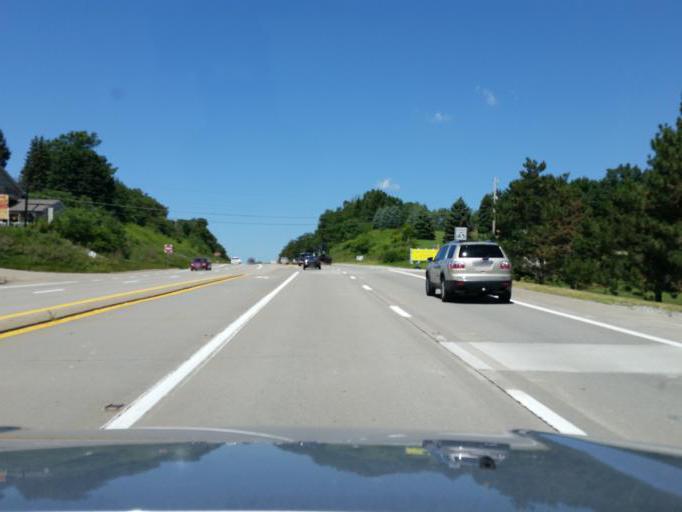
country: US
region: Pennsylvania
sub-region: Westmoreland County
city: Delmont
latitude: 40.4011
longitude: -79.5126
